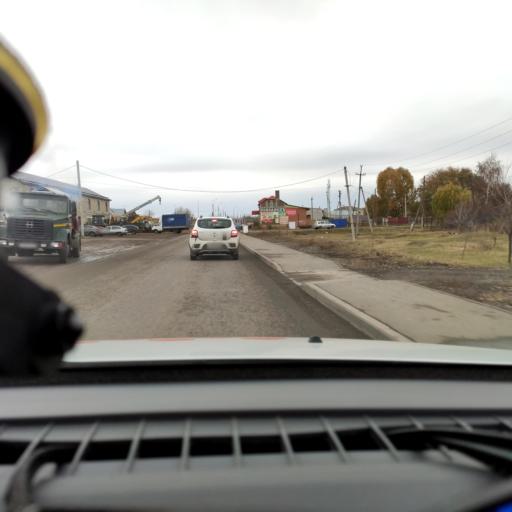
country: RU
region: Samara
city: Samara
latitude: 53.1321
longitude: 50.2359
